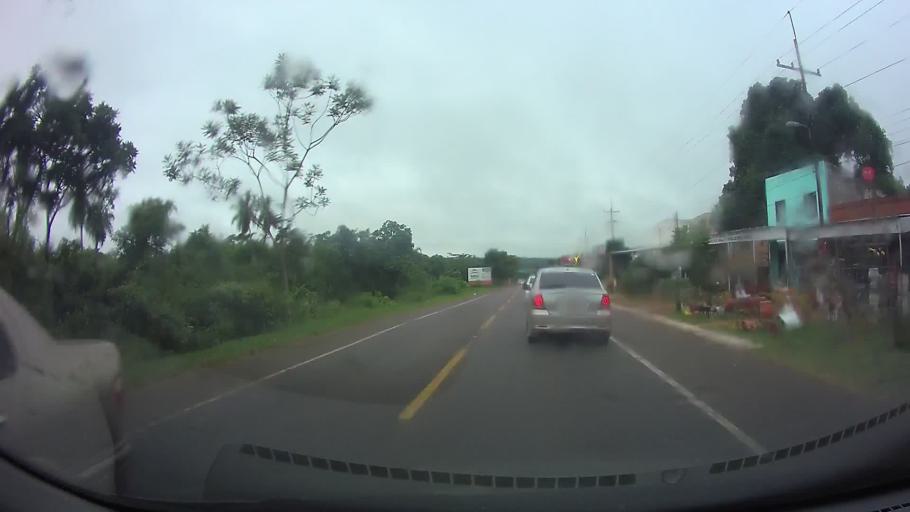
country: PY
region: Central
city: Ita
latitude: -25.5360
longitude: -57.3258
